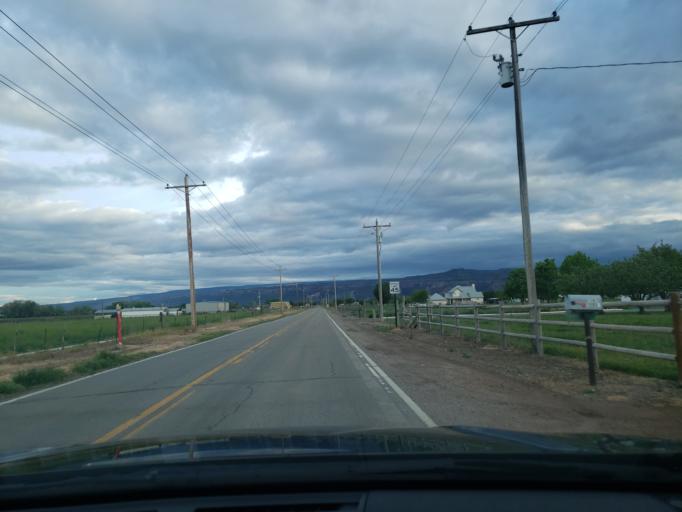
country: US
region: Colorado
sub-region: Mesa County
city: Fruita
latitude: 39.1926
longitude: -108.7013
